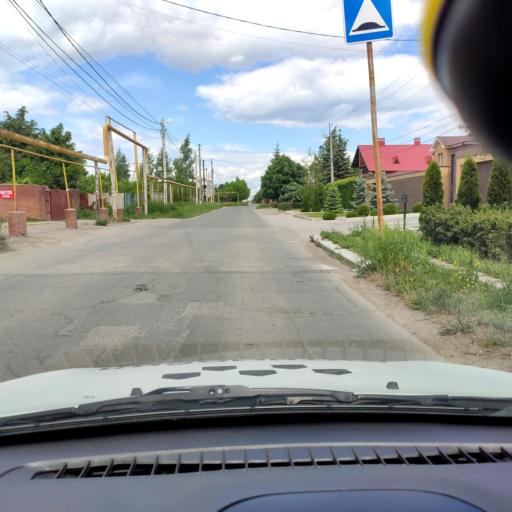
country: RU
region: Samara
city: Podstepki
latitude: 53.5175
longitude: 49.1626
